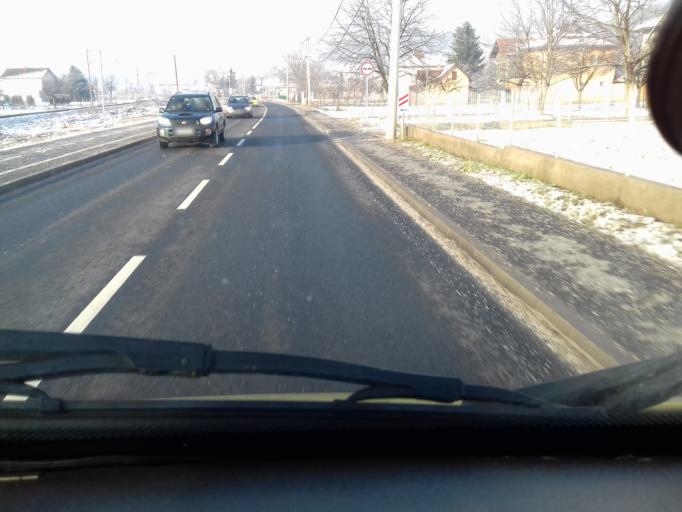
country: BA
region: Federation of Bosnia and Herzegovina
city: Mahala
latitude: 43.9819
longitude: 18.2396
